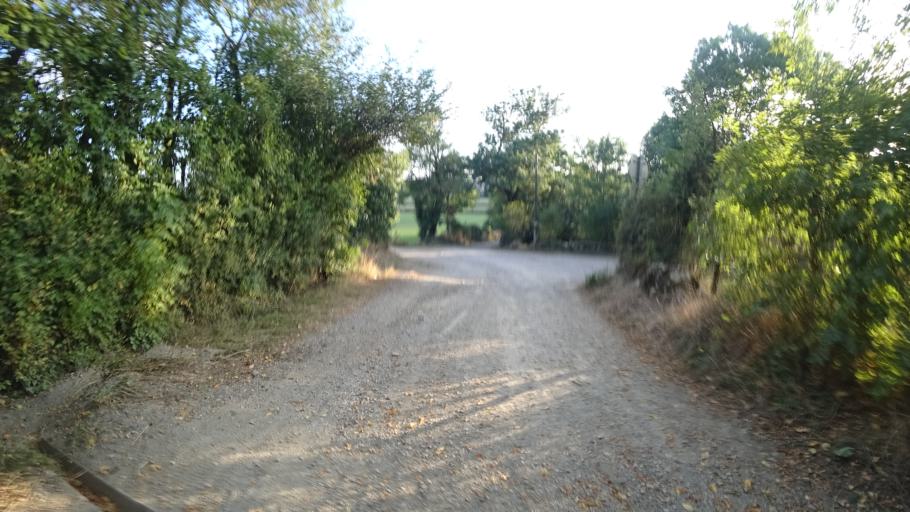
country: FR
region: Midi-Pyrenees
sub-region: Departement de l'Aveyron
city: Sebazac-Concoures
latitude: 44.3897
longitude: 2.5876
